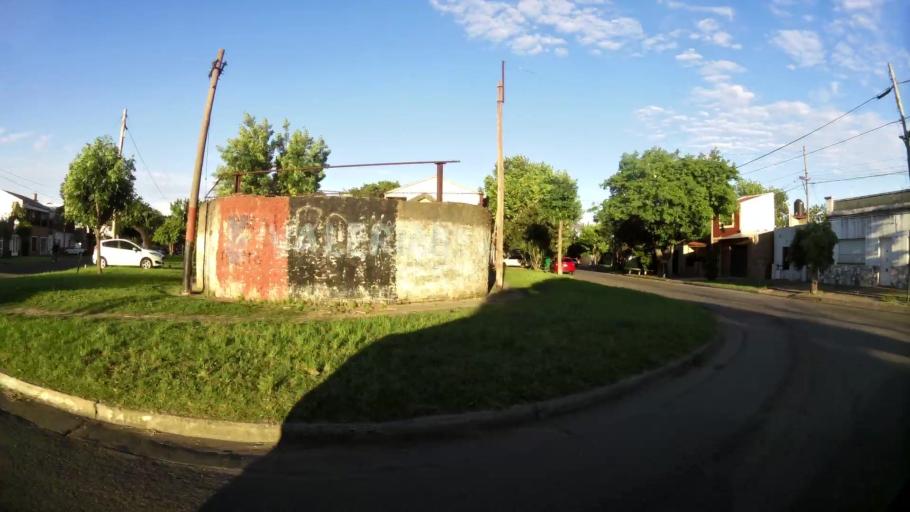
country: AR
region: Santa Fe
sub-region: Departamento de Rosario
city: Rosario
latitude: -32.9723
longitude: -60.6726
